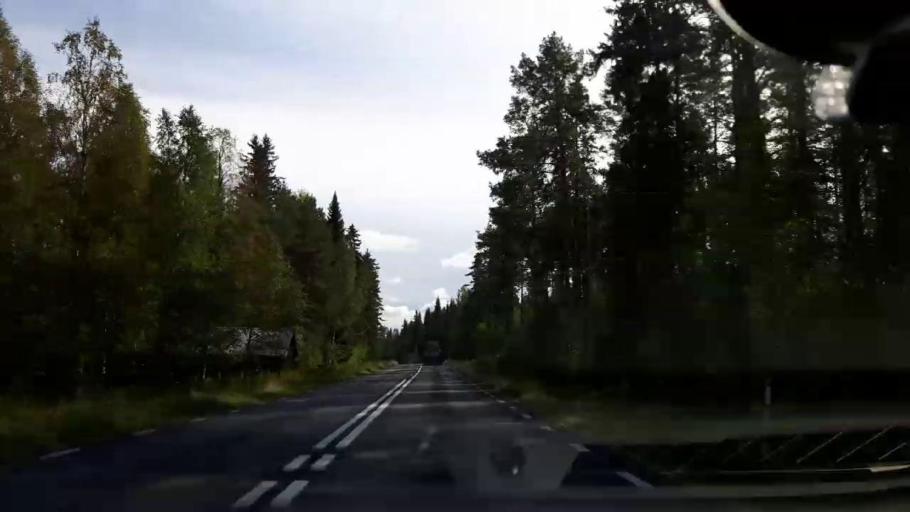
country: SE
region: Jaemtland
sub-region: Braecke Kommun
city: Braecke
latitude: 63.1704
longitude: 15.5460
